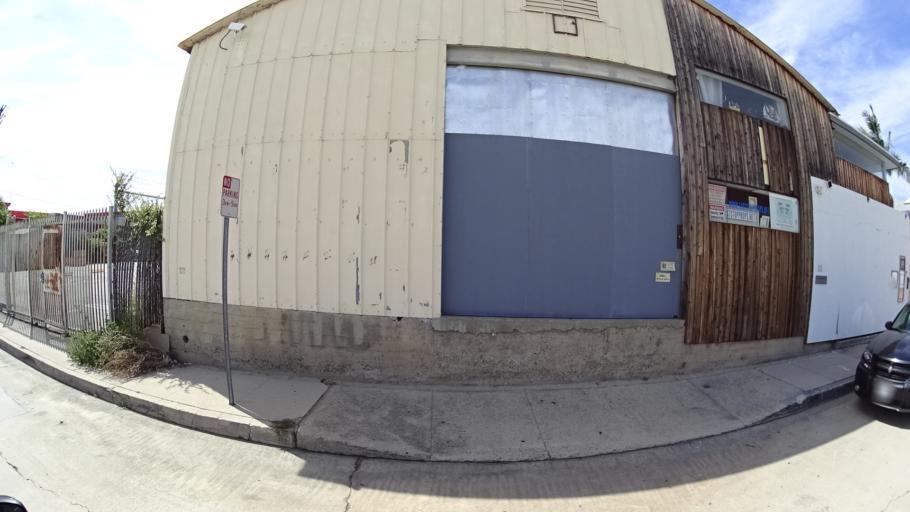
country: US
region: California
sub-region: Los Angeles County
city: Burbank
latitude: 34.1719
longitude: -118.2983
